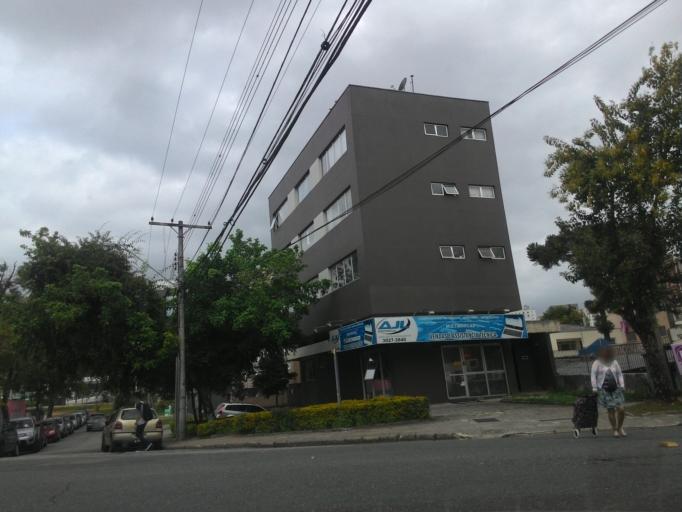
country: BR
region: Parana
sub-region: Curitiba
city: Curitiba
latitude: -25.4156
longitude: -49.2715
